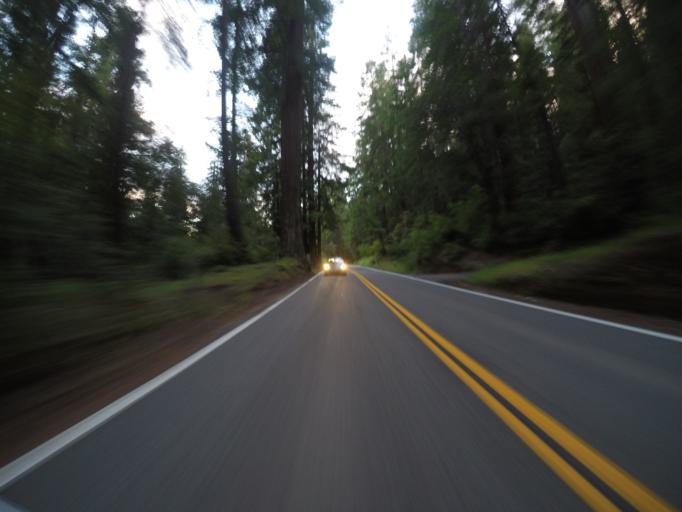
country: US
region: California
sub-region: Humboldt County
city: Redway
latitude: 40.0269
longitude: -123.7937
